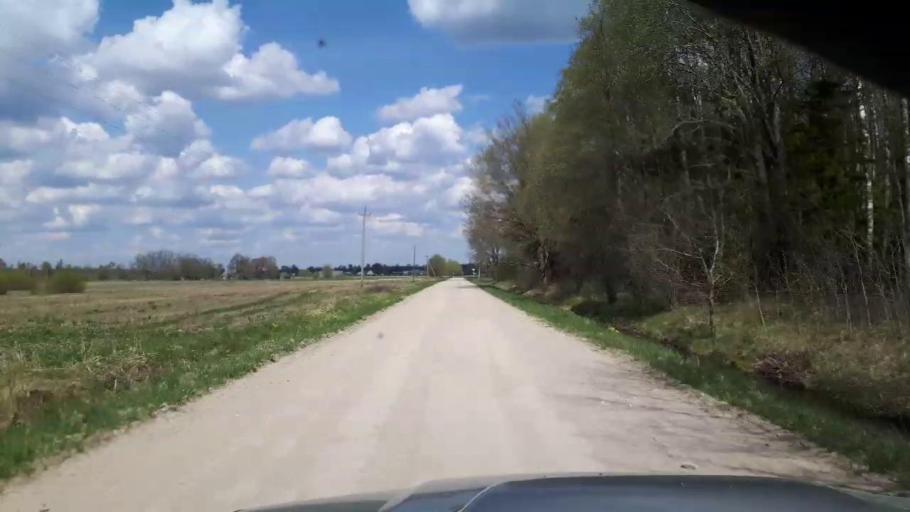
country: EE
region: Paernumaa
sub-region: Tootsi vald
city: Tootsi
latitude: 58.4817
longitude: 24.9016
